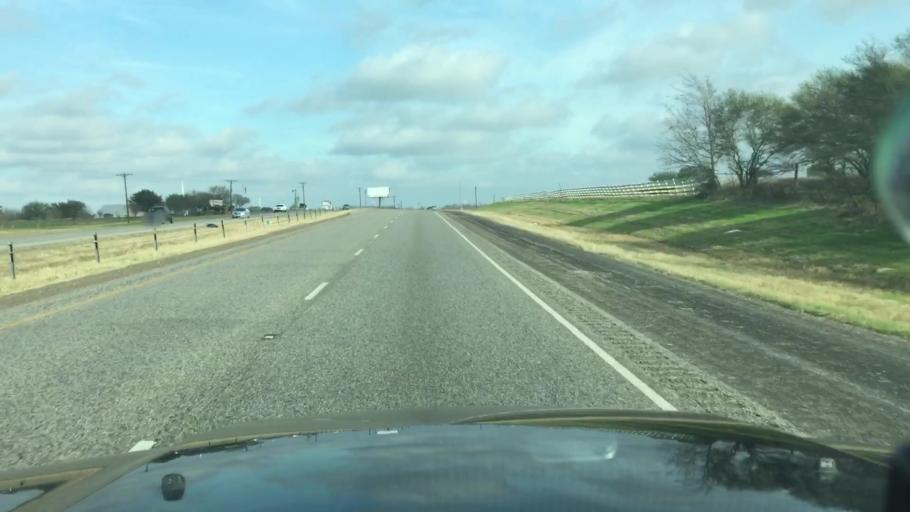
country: US
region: Texas
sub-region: Washington County
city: Brenham
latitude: 30.1412
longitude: -96.2865
